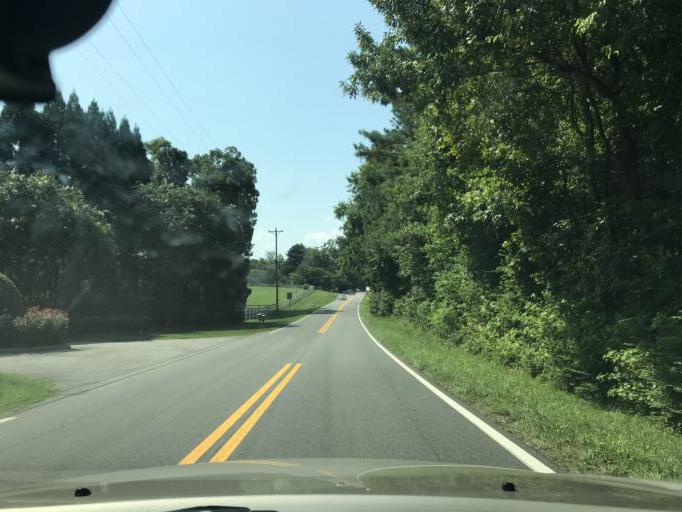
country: US
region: Georgia
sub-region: Hall County
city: Flowery Branch
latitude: 34.2448
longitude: -83.9973
